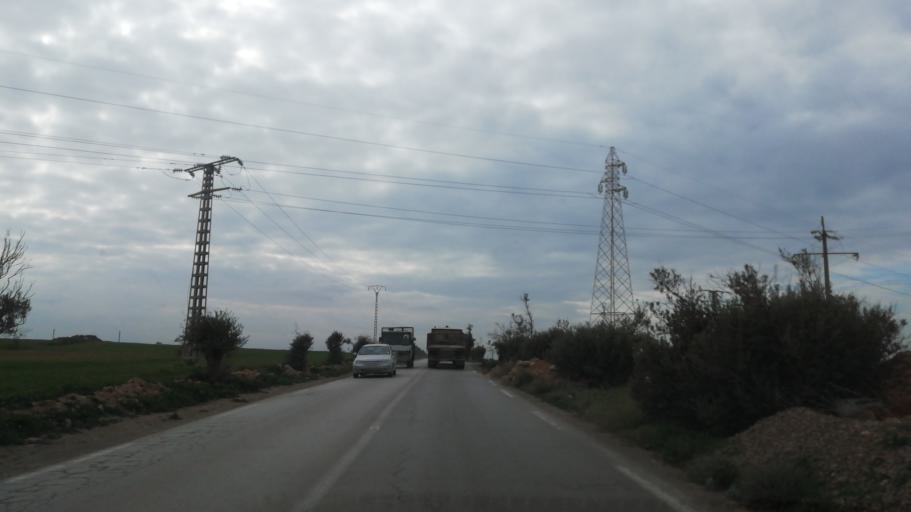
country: DZ
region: Oran
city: Ain el Bya
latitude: 35.7872
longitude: -0.3431
